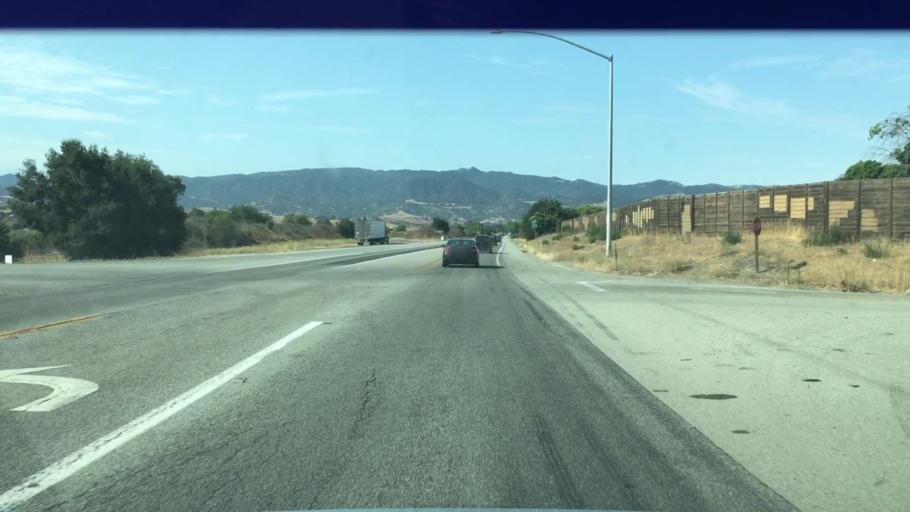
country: US
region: California
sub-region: San Benito County
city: Hollister
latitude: 36.8639
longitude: -121.4440
